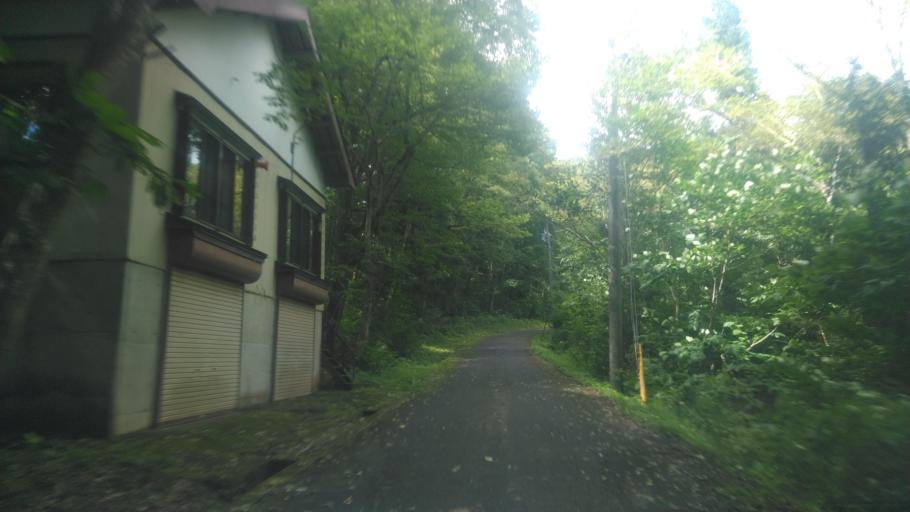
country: JP
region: Niigata
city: Arai
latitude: 36.8397
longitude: 138.1699
